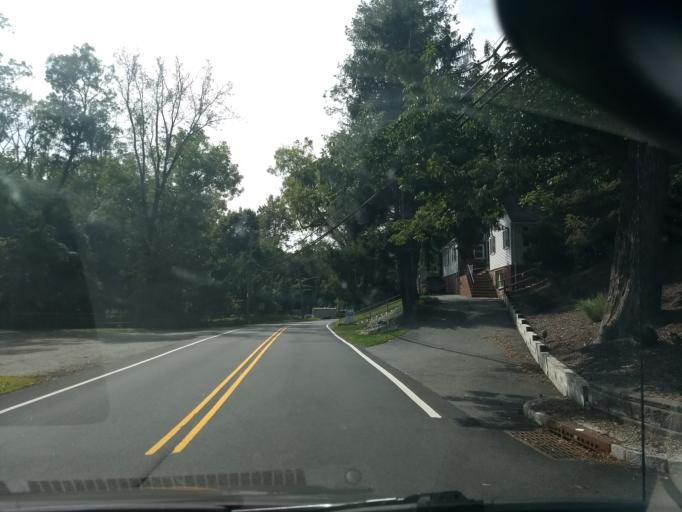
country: US
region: New Jersey
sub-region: Morris County
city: Morris Plains
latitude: 40.8200
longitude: -74.4940
